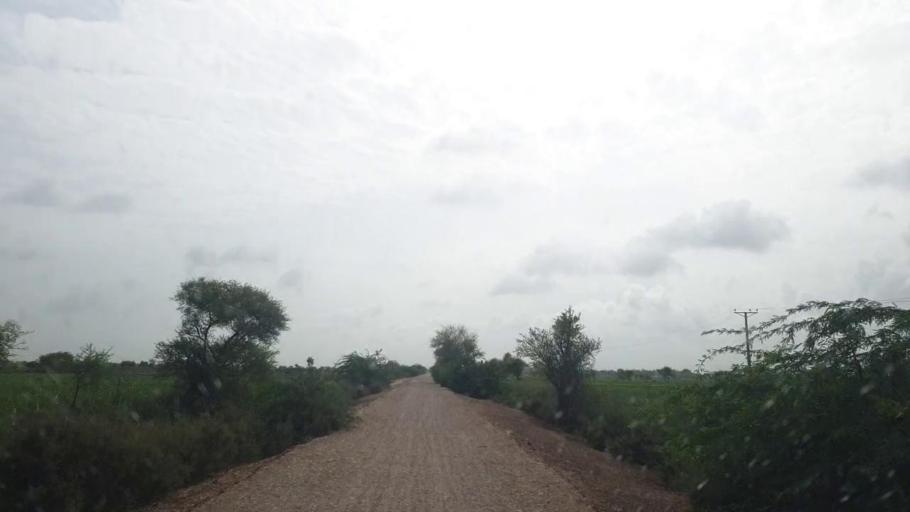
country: PK
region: Sindh
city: Tando Bago
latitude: 24.8022
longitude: 69.0083
